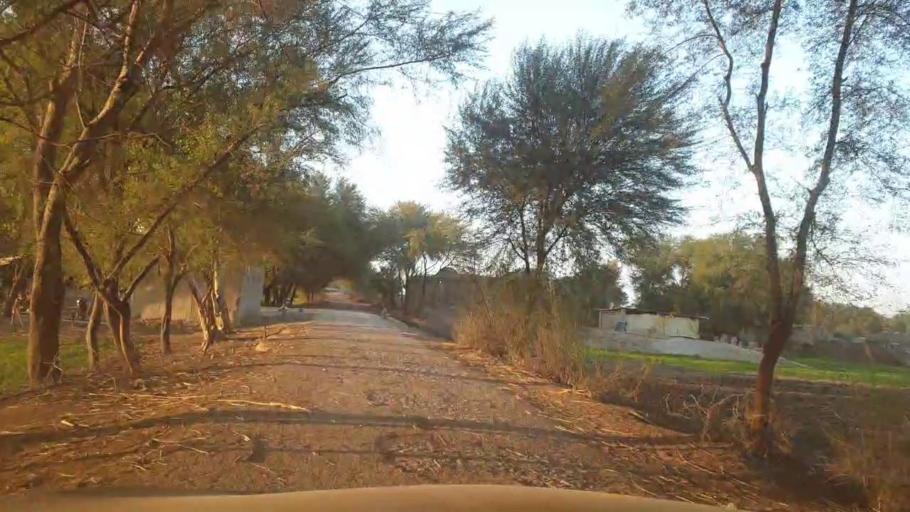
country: PK
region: Sindh
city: Ubauro
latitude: 28.1867
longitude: 69.6019
